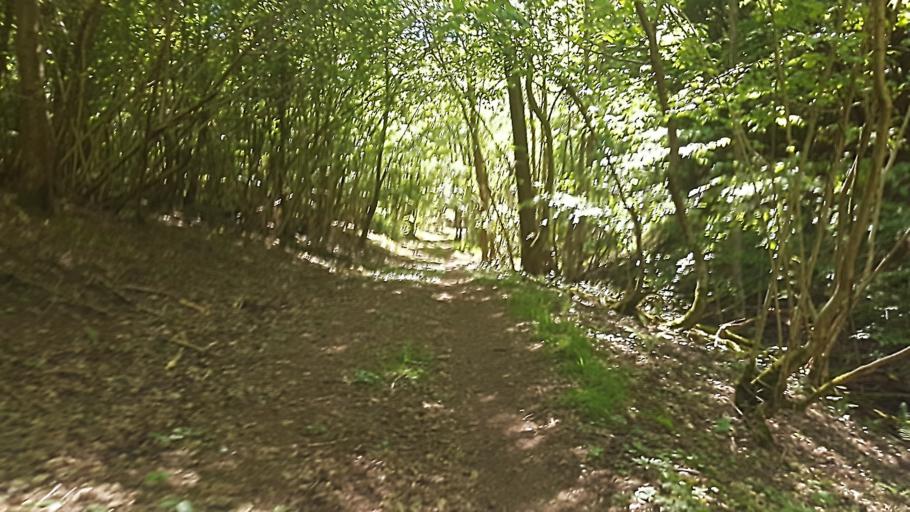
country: BE
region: Wallonia
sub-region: Province de Namur
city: Couvin
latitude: 50.0596
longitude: 4.5766
